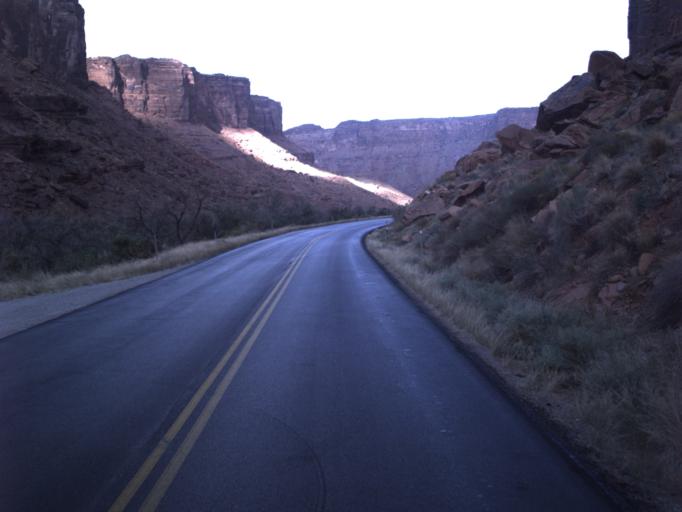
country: US
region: Utah
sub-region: Grand County
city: Moab
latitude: 38.6256
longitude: -109.5097
